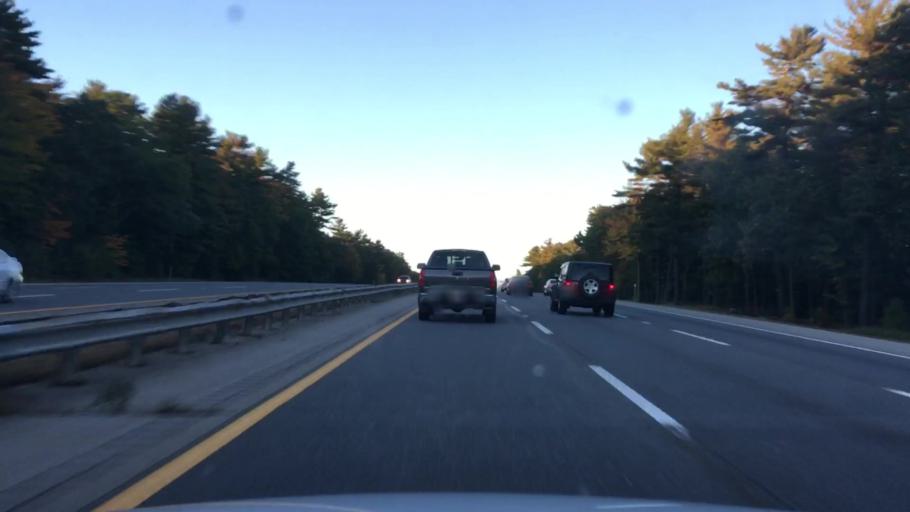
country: US
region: Maine
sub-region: York County
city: Ogunquit
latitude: 43.2766
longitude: -70.6180
